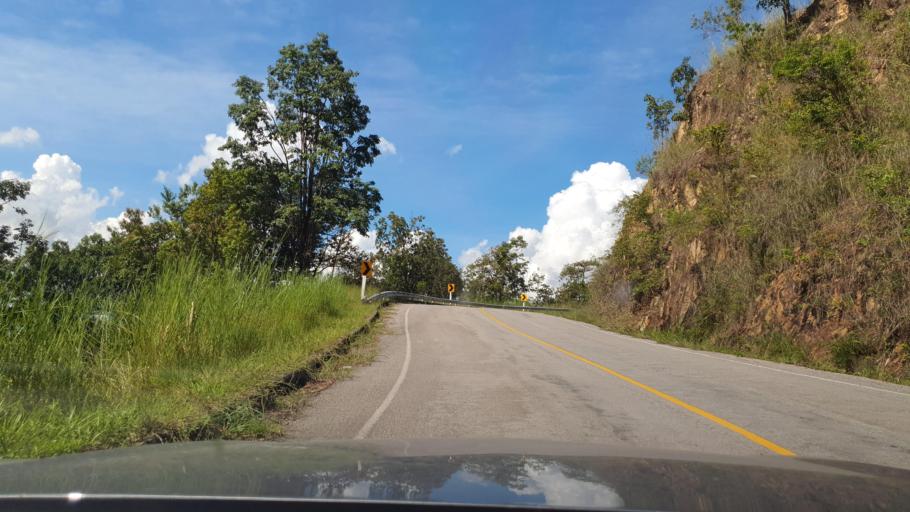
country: TH
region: Chiang Mai
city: Phrao
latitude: 19.3614
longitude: 99.2724
